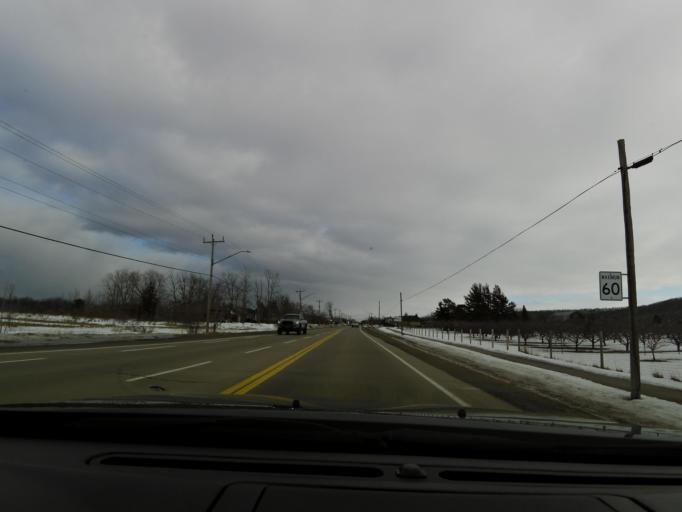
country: CA
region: Ontario
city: Hamilton
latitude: 43.2094
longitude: -79.6601
